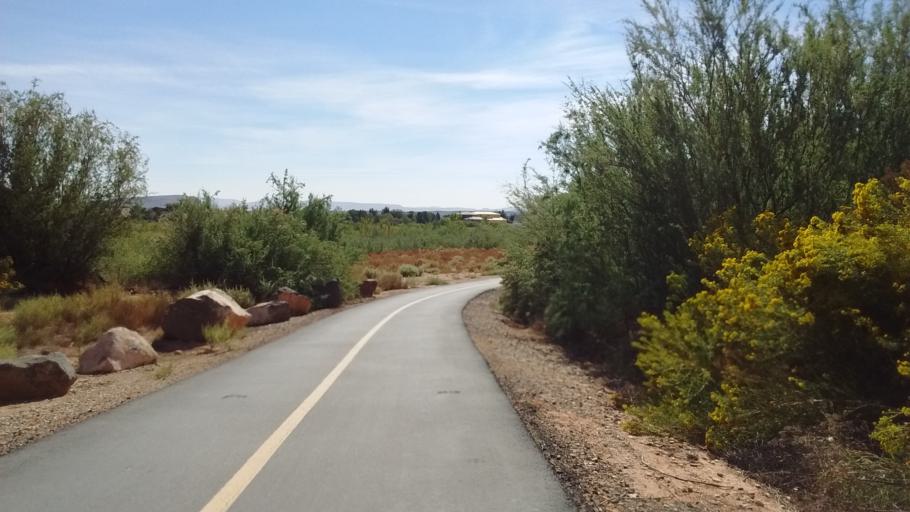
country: US
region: Utah
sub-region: Washington County
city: Washington
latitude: 37.1033
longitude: -113.5283
